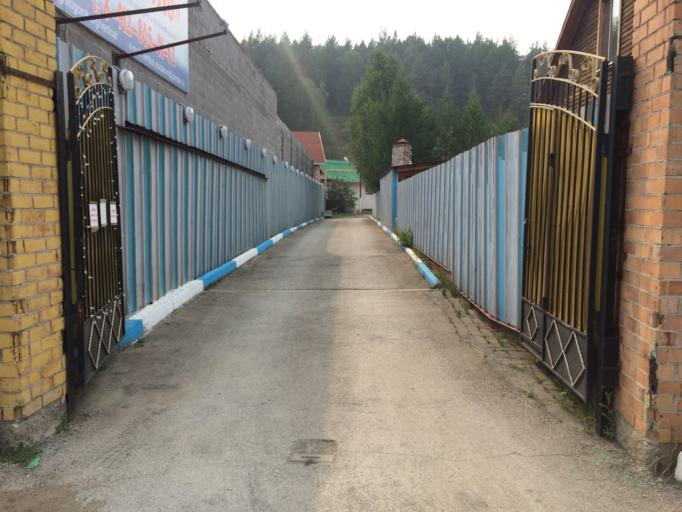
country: RU
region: Bashkortostan
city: Abzakovo
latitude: 53.8074
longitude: 58.6361
